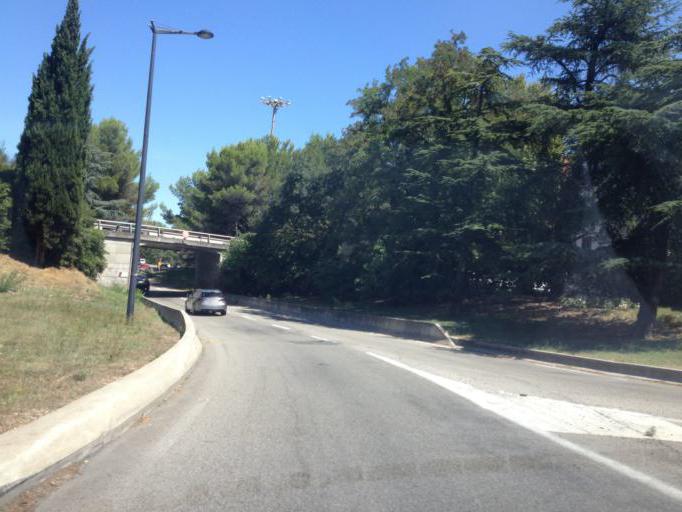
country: FR
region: Provence-Alpes-Cote d'Azur
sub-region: Departement du Vaucluse
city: Avignon
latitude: 43.9427
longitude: 4.7948
